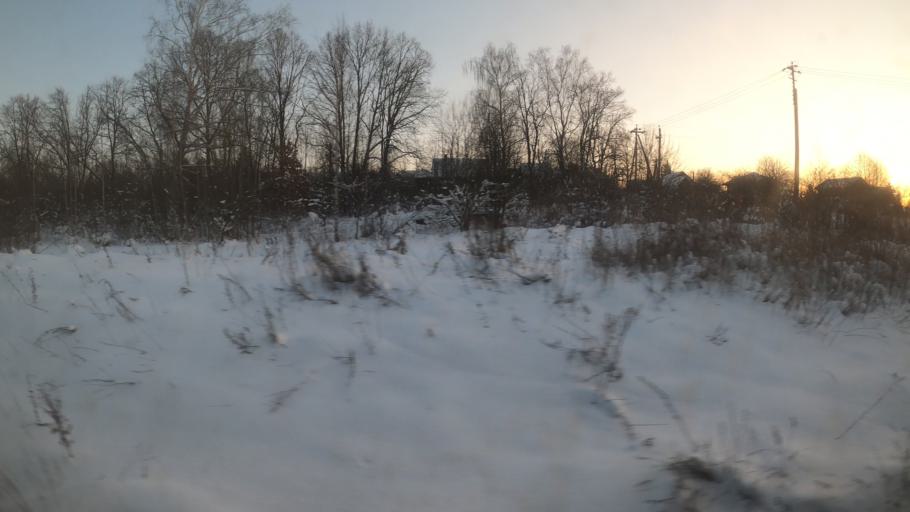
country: RU
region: Moskovskaya
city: Dedenevo
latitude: 56.2520
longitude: 37.5054
